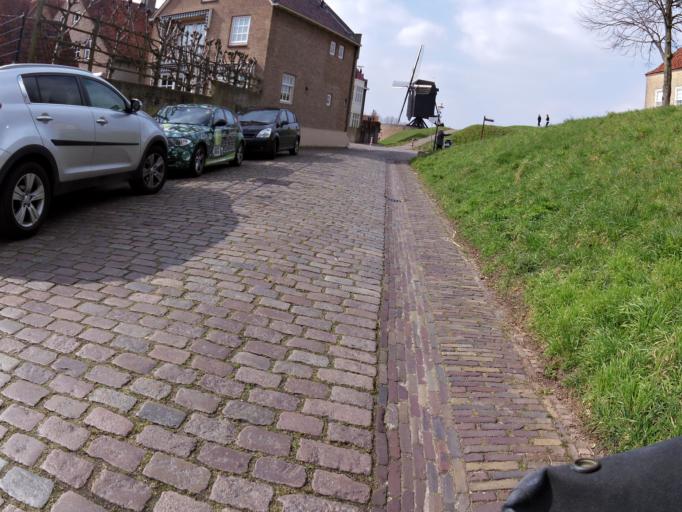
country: NL
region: North Brabant
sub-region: Gemeente Heusden
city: Heusden
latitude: 51.7359
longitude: 5.1408
